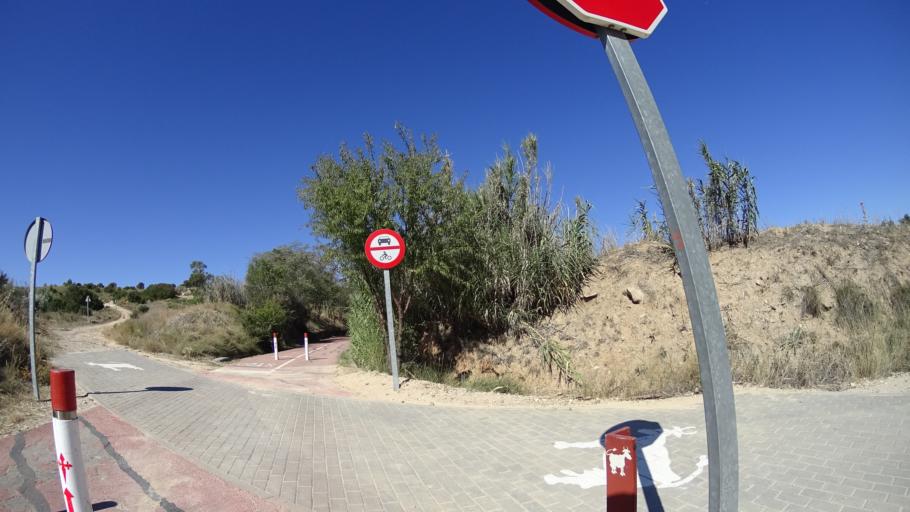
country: ES
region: Madrid
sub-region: Provincia de Madrid
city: Arganda
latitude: 40.2659
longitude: -3.4614
